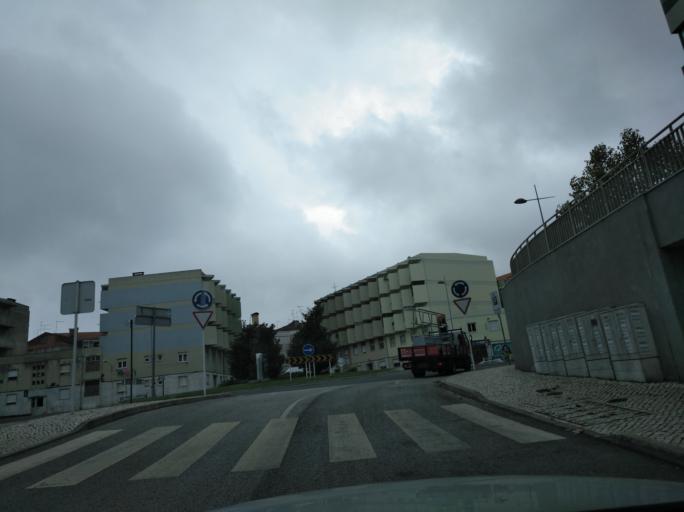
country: PT
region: Lisbon
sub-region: Loures
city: Moscavide
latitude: 38.7808
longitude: -9.1018
